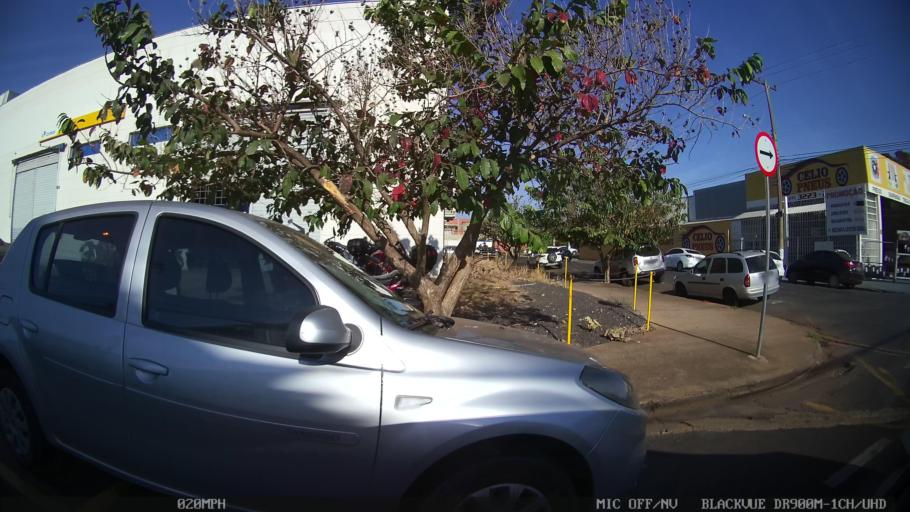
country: BR
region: Sao Paulo
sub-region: Sao Jose Do Rio Preto
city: Sao Jose do Rio Preto
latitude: -20.7928
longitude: -49.3624
